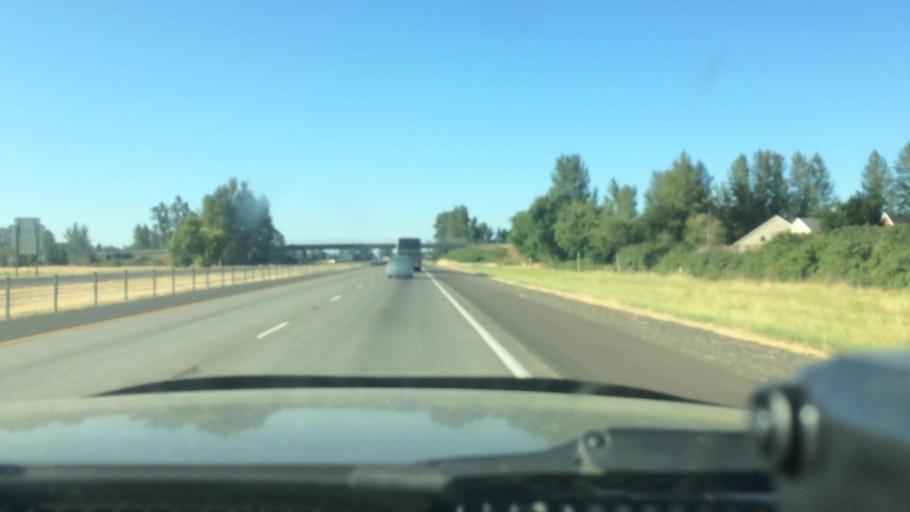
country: US
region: Oregon
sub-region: Linn County
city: Albany
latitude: 44.6139
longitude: -123.0623
